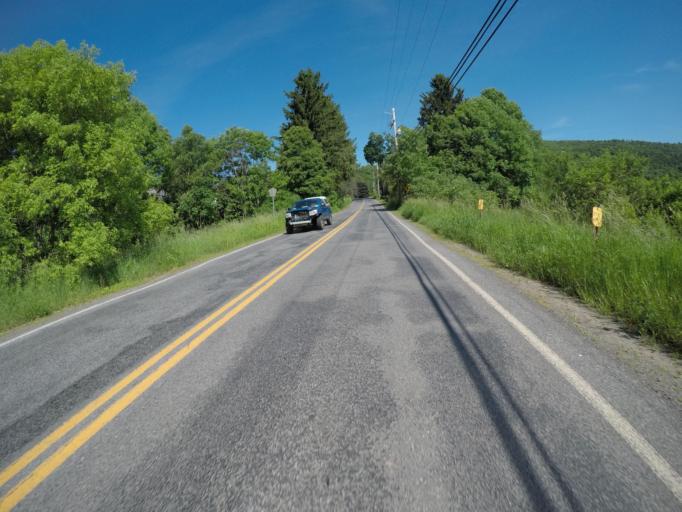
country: US
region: New York
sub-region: Delaware County
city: Delhi
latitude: 42.2103
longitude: -74.9782
